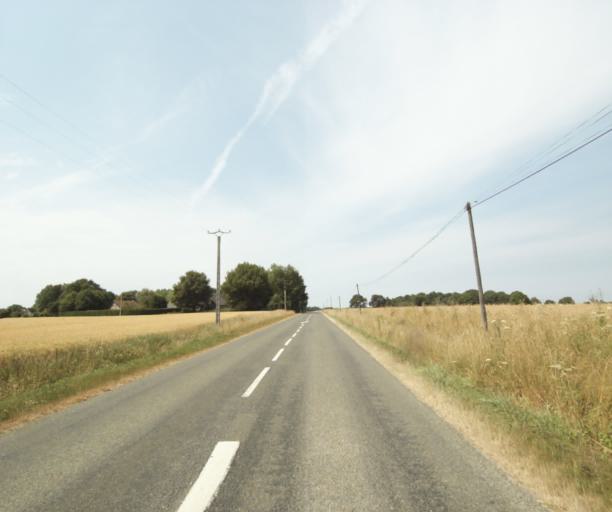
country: FR
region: Centre
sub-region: Departement d'Eure-et-Loir
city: Unverre
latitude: 48.1840
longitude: 1.0418
